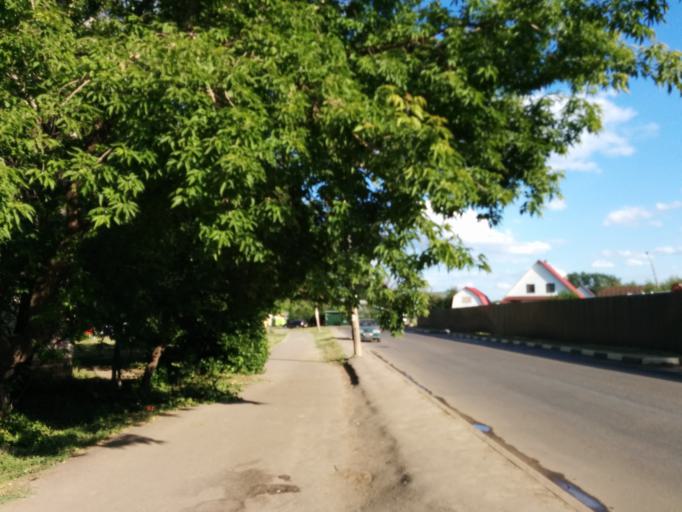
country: RU
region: Tambov
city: Tambov
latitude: 52.7534
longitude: 41.4352
